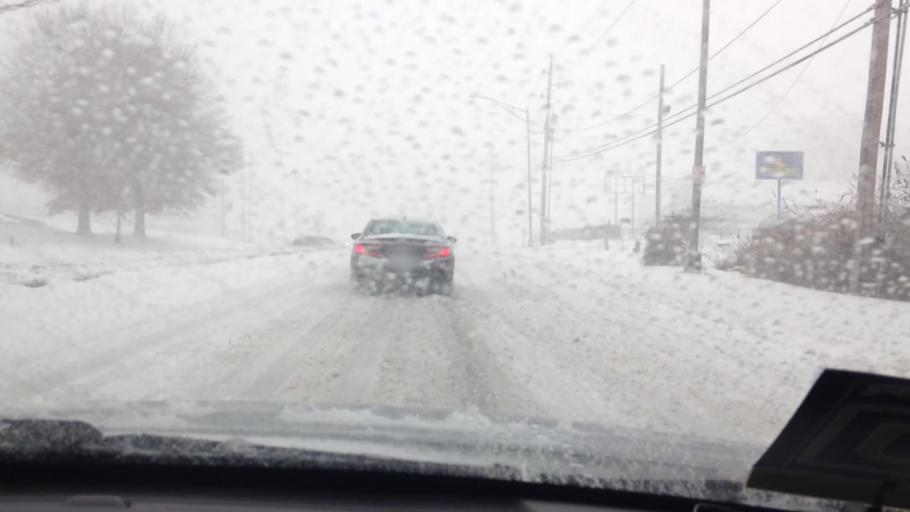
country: US
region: Kansas
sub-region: Wyandotte County
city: Kansas City
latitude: 39.1166
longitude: -94.6963
